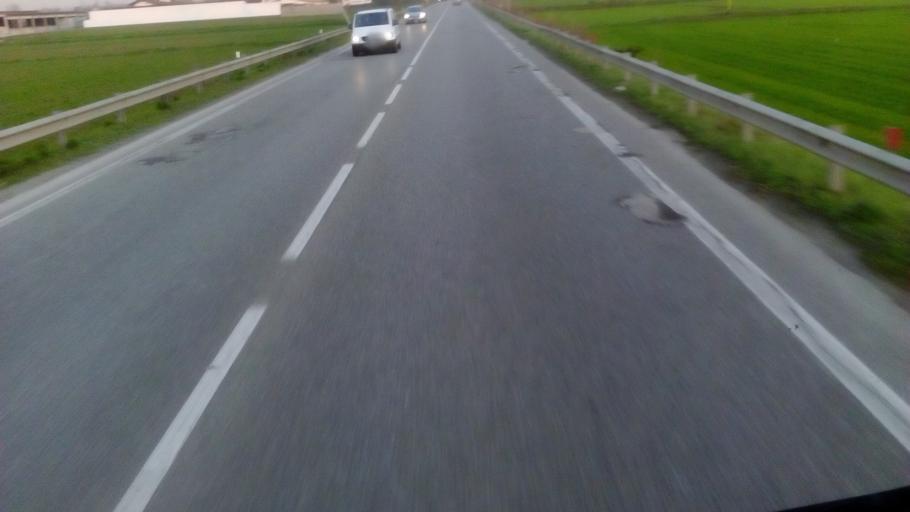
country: IT
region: Lombardy
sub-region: Provincia di Brescia
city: Orzinuovi
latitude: 45.4150
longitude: 9.9157
